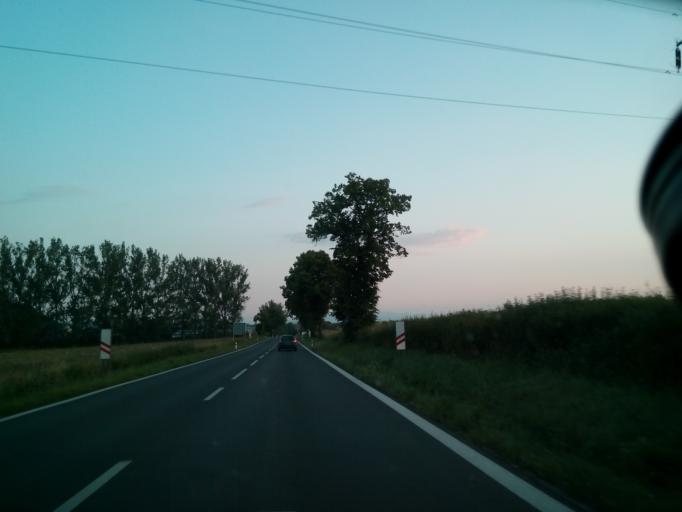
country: SK
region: Presovsky
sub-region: Okres Presov
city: Kezmarok
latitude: 49.1559
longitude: 20.4371
